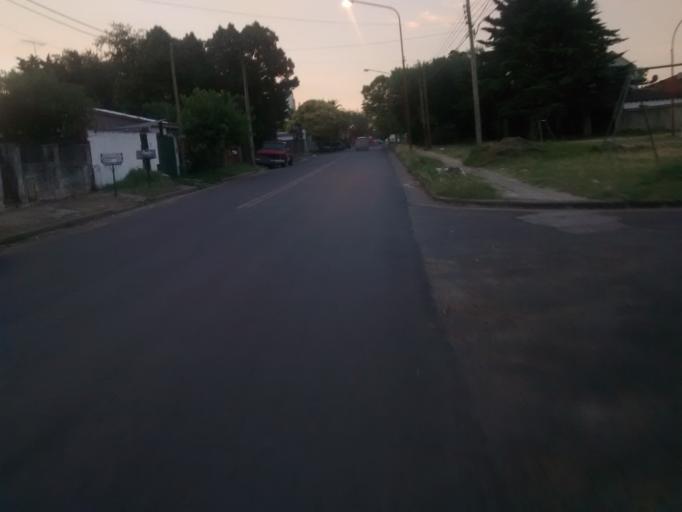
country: AR
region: Buenos Aires
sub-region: Partido de La Plata
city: La Plata
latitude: -34.9415
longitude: -57.9263
